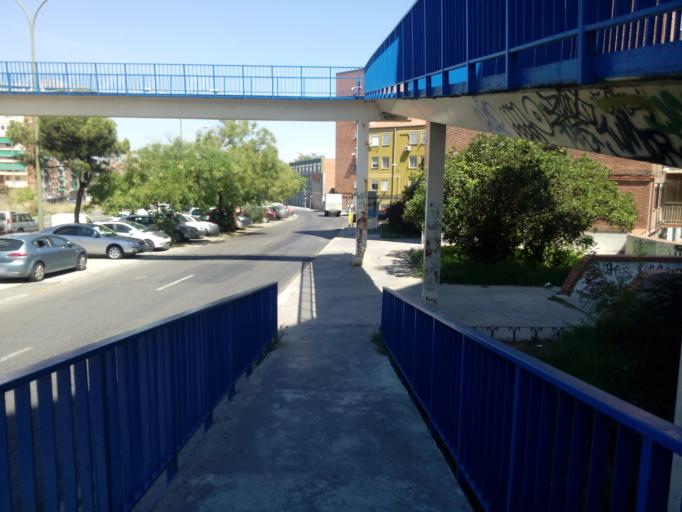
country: ES
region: Madrid
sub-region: Provincia de Madrid
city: Usera
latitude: 40.3913
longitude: -3.7081
